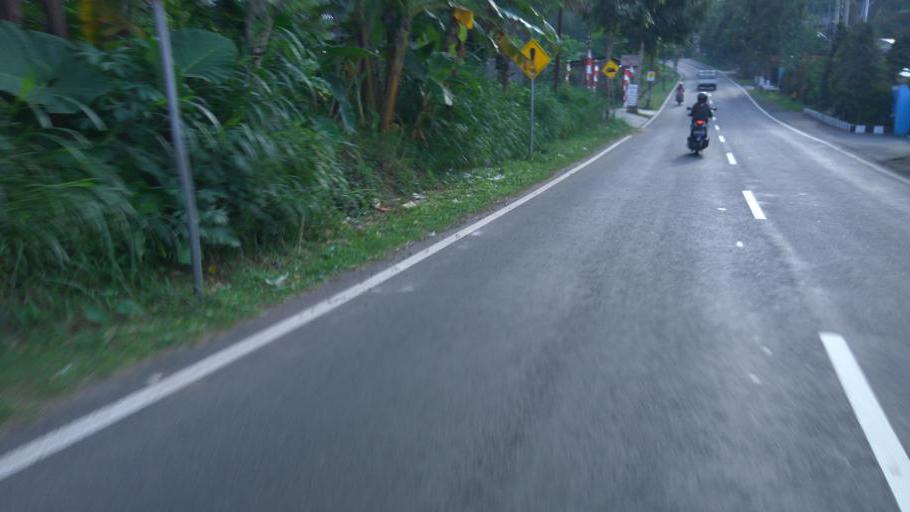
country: ID
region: Central Java
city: Salatiga
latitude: -7.3648
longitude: 110.4727
